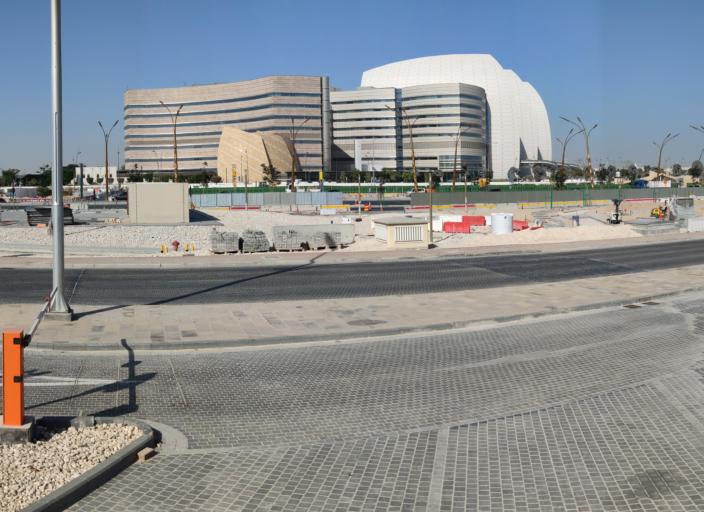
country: QA
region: Baladiyat ar Rayyan
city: Ar Rayyan
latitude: 25.3189
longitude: 51.4428
